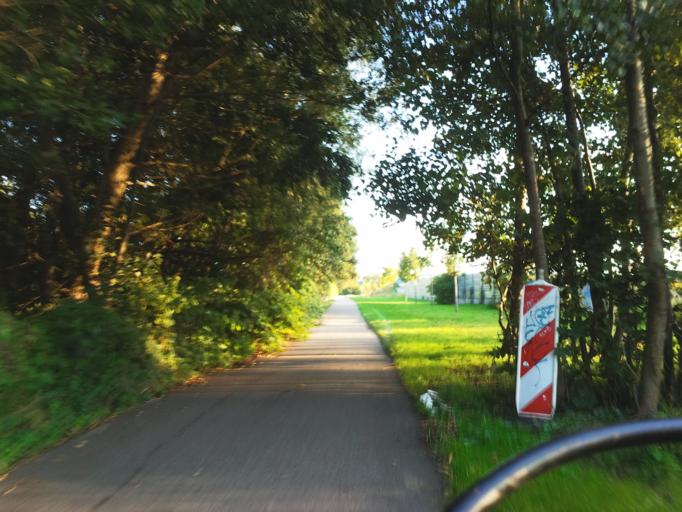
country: DE
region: Mecklenburg-Vorpommern
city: Kritzmow
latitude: 54.0893
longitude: 12.0678
